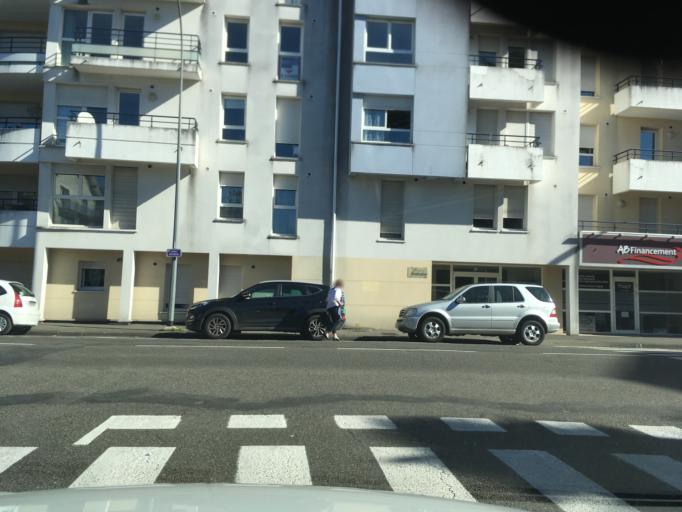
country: FR
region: Aquitaine
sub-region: Departement des Pyrenees-Atlantiques
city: Pau
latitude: 43.3091
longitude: -0.3770
